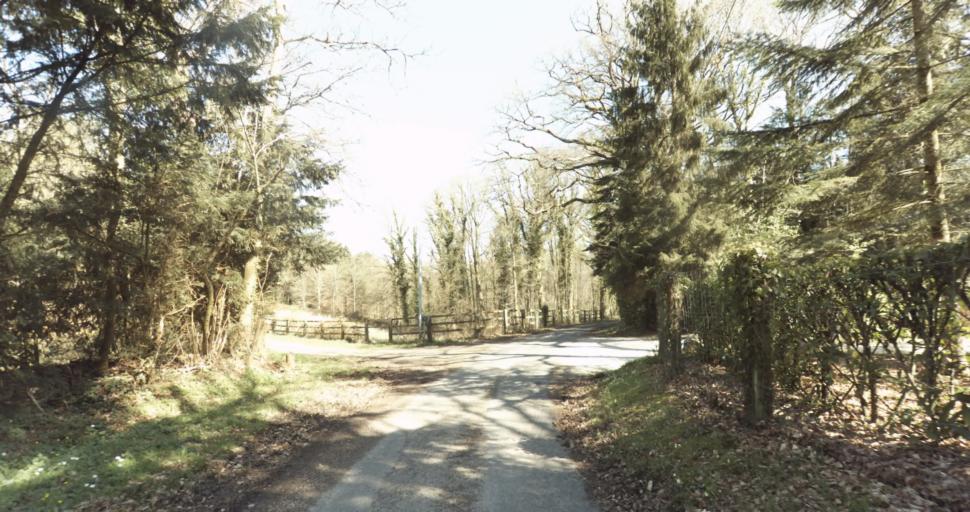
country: FR
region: Lower Normandy
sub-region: Departement du Calvados
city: Livarot
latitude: 49.0050
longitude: 0.0624
